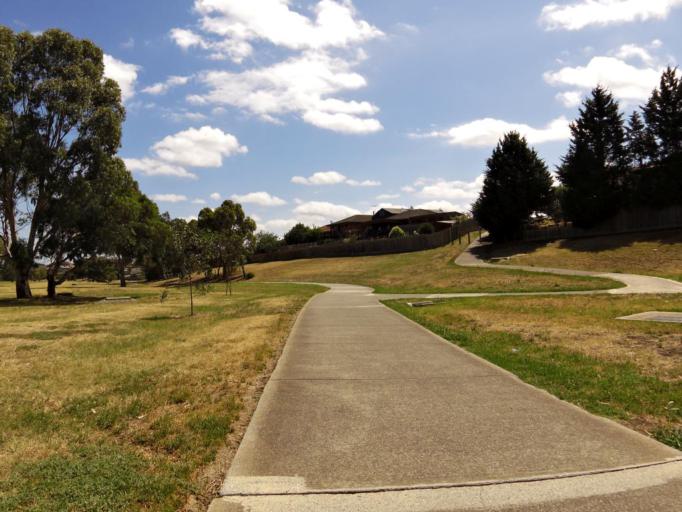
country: AU
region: Victoria
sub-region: Hume
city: Meadow Heights
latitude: -37.6442
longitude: 144.9204
